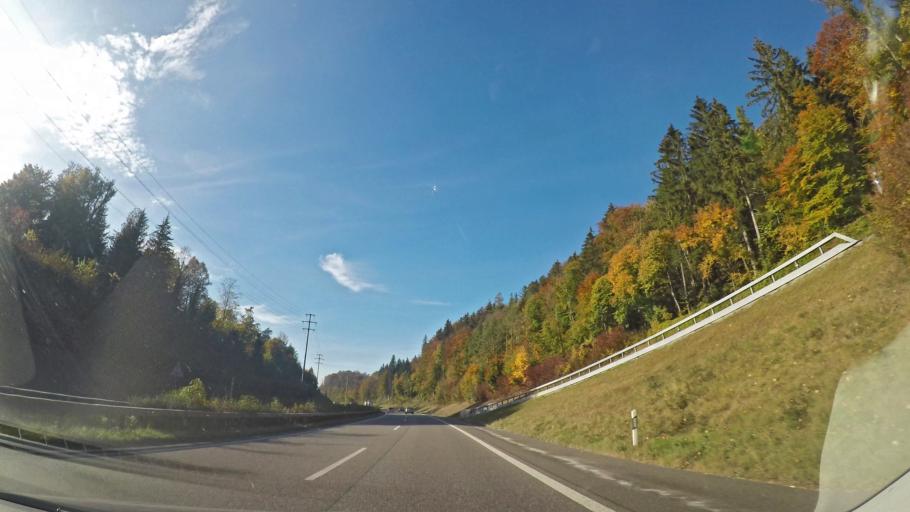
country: CH
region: Bern
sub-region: Frutigen-Niedersimmental District
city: Wimmis
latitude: 46.7107
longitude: 7.6309
